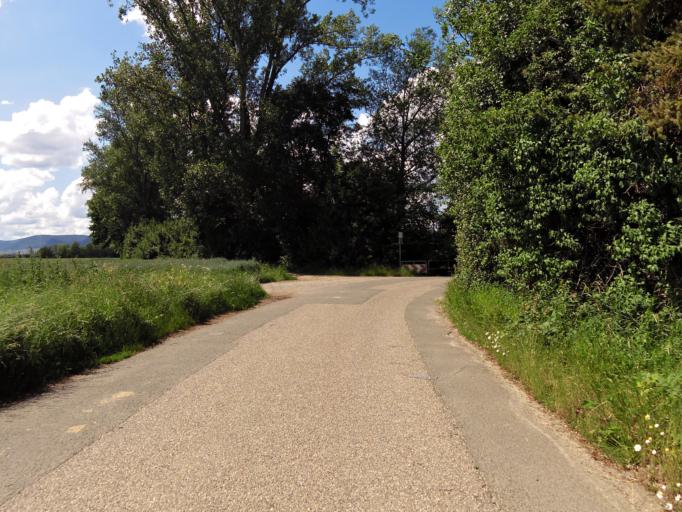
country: DE
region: Rheinland-Pfalz
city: Altdorf
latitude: 49.2823
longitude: 8.2214
